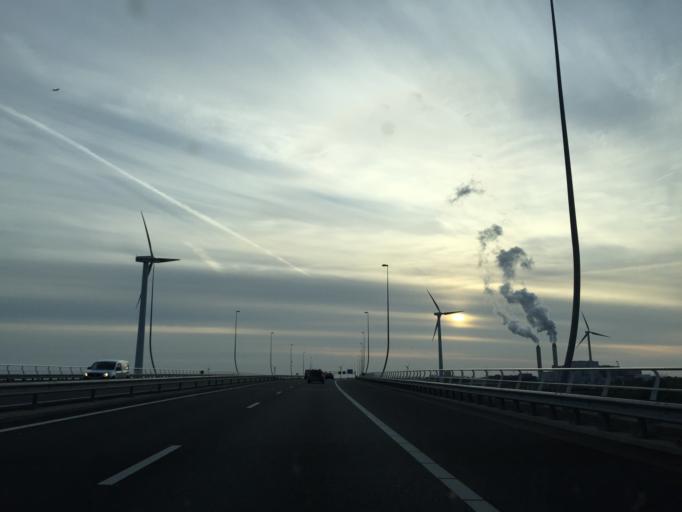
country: NL
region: North Holland
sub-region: Gemeente Zaanstad
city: Zaandam
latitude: 52.3922
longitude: 4.8123
